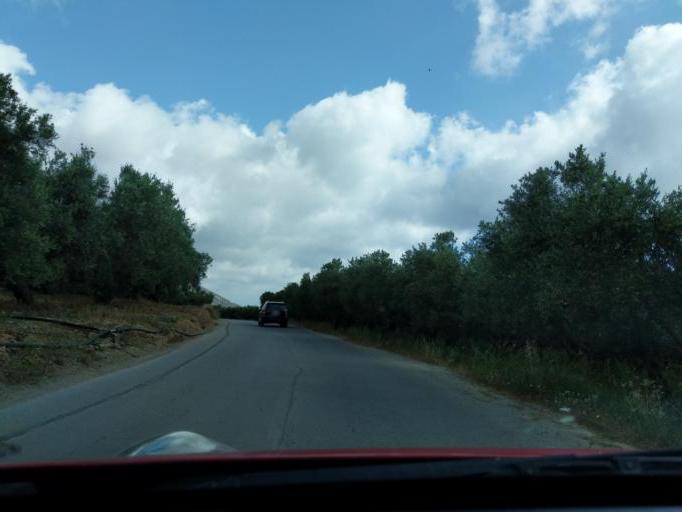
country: GR
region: Crete
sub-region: Nomos Chanias
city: Platanos
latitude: 35.5059
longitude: 23.6142
